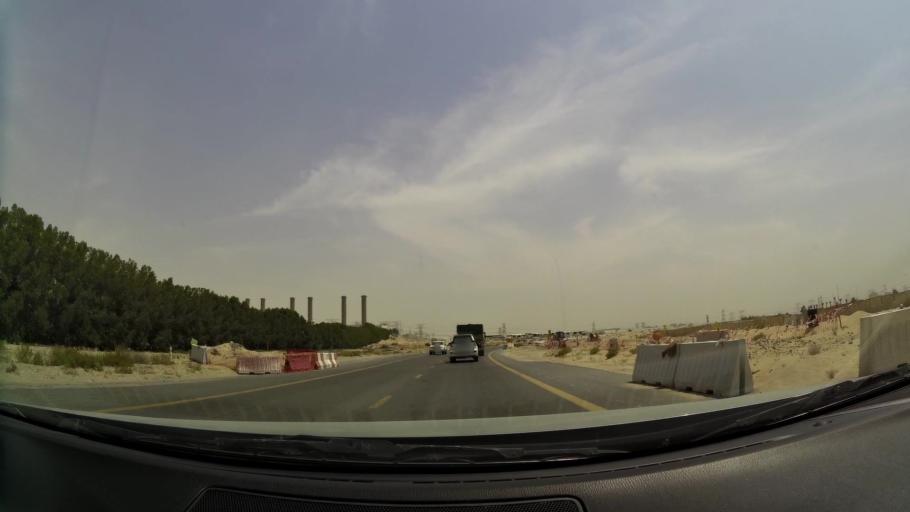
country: AE
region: Ash Shariqah
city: Sharjah
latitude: 25.1556
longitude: 55.4238
